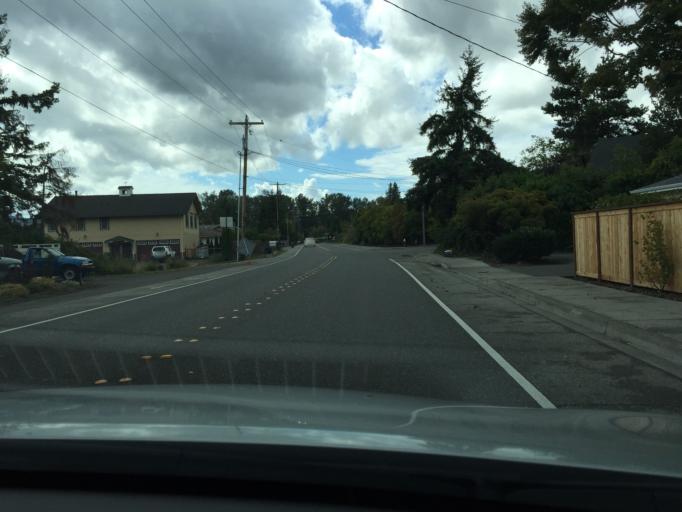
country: US
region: Washington
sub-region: Whatcom County
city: Geneva
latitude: 48.7654
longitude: -122.4181
